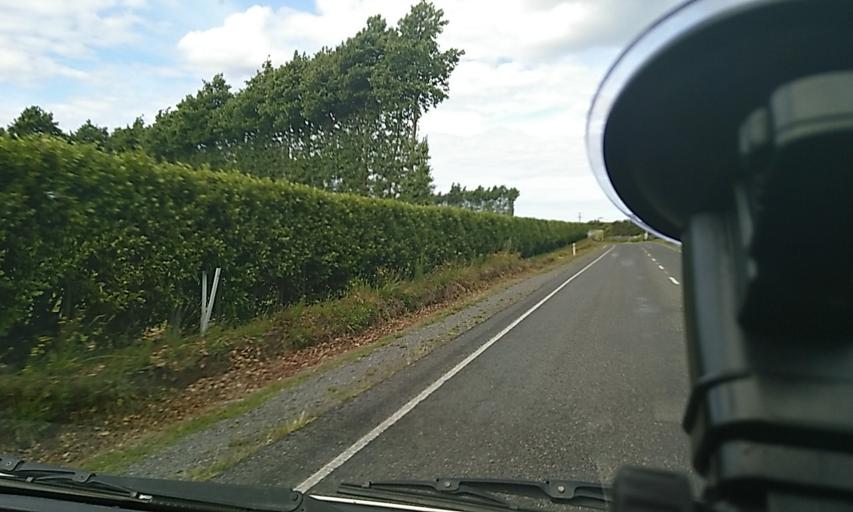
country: NZ
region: Bay of Plenty
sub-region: Western Bay of Plenty District
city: Waihi Beach
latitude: -37.4493
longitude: 175.9515
